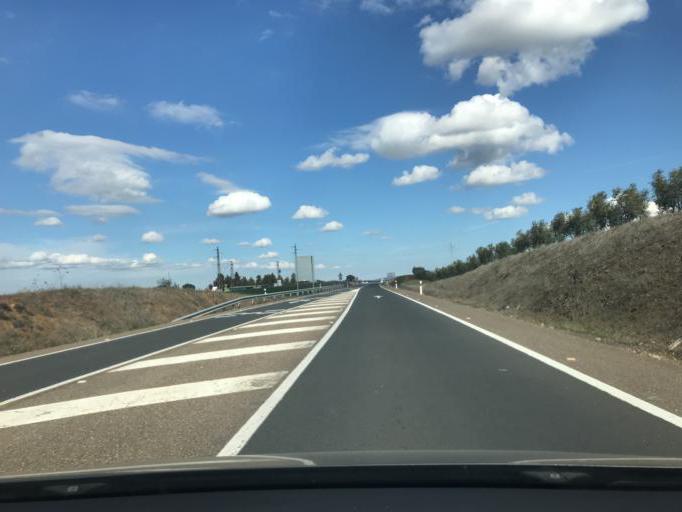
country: ES
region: Extremadura
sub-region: Provincia de Badajoz
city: Azuaga
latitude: 38.2713
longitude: -5.6850
